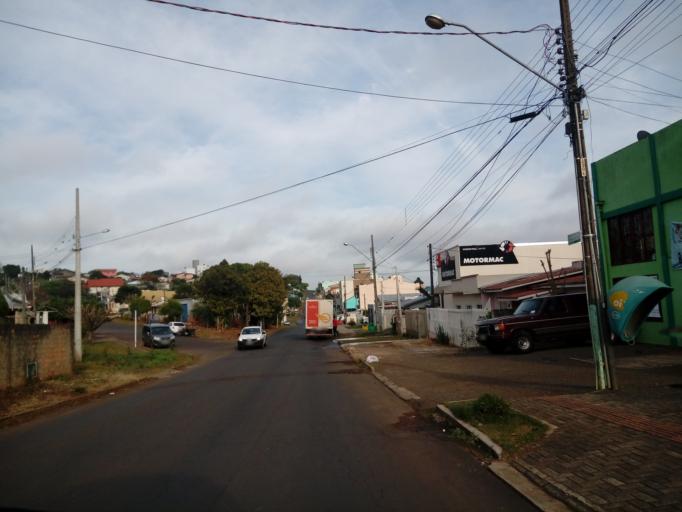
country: BR
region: Santa Catarina
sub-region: Chapeco
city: Chapeco
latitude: -27.0722
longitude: -52.6300
